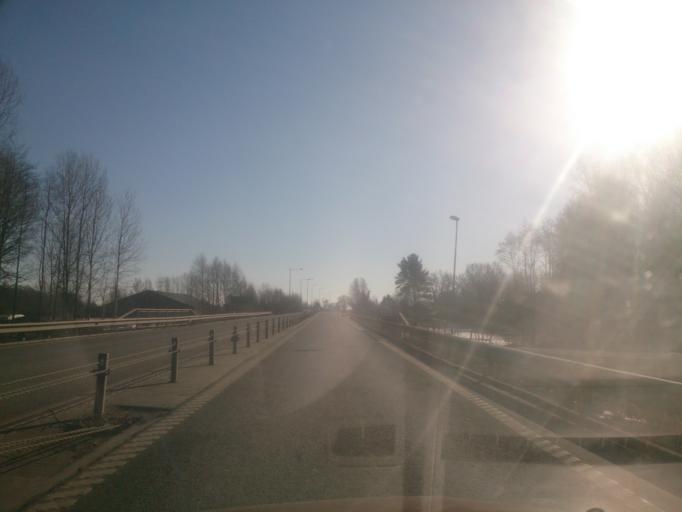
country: SE
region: OEstergoetland
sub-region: Norrkopings Kommun
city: Jursla
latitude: 58.6610
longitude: 16.1687
